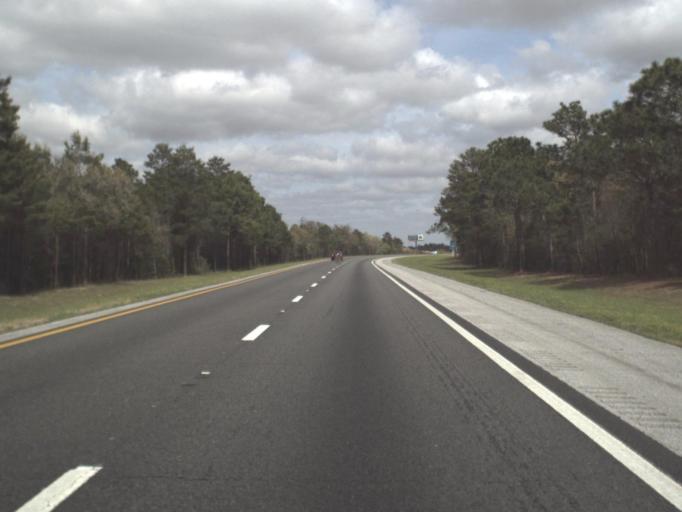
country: US
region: Florida
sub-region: Okaloosa County
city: Crestview
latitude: 30.7328
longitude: -86.3755
